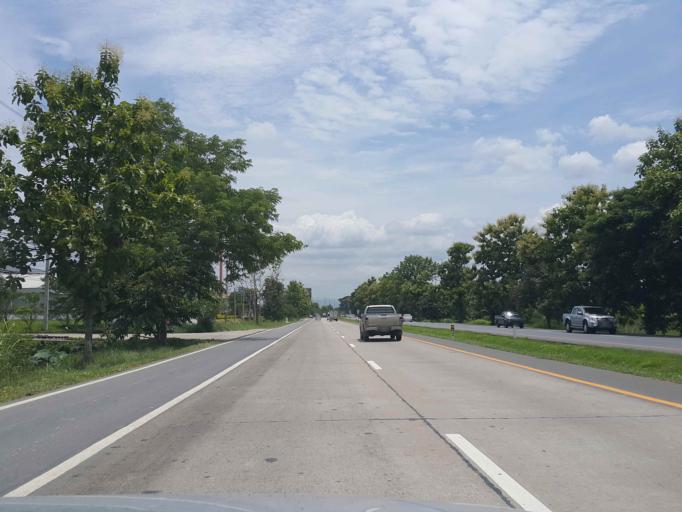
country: TH
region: Chiang Mai
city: Saraphi
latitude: 18.6511
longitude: 99.0531
